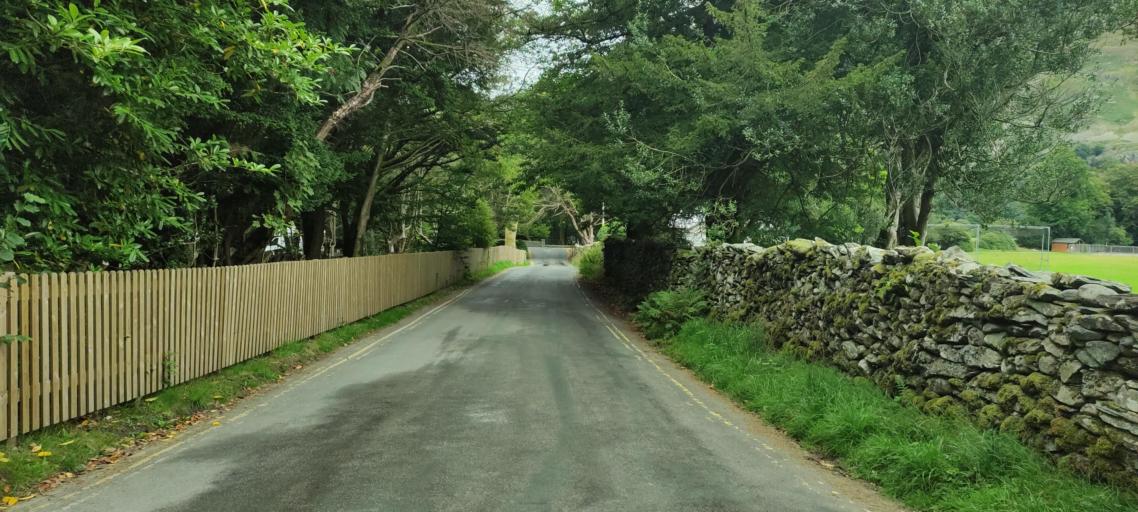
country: GB
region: England
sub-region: Cumbria
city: Ambleside
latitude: 54.5358
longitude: -2.9444
